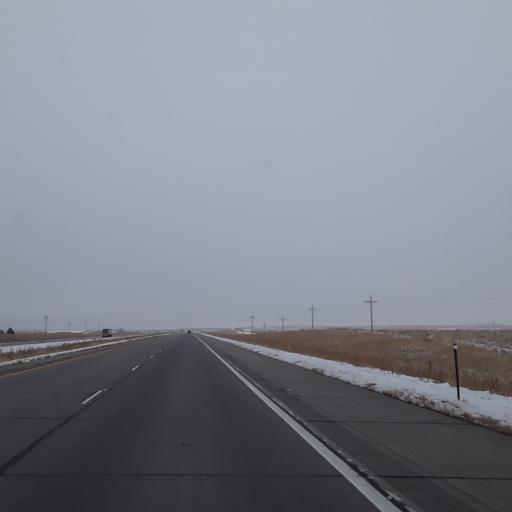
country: US
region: Colorado
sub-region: Logan County
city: Sterling
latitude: 40.5280
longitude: -103.2347
